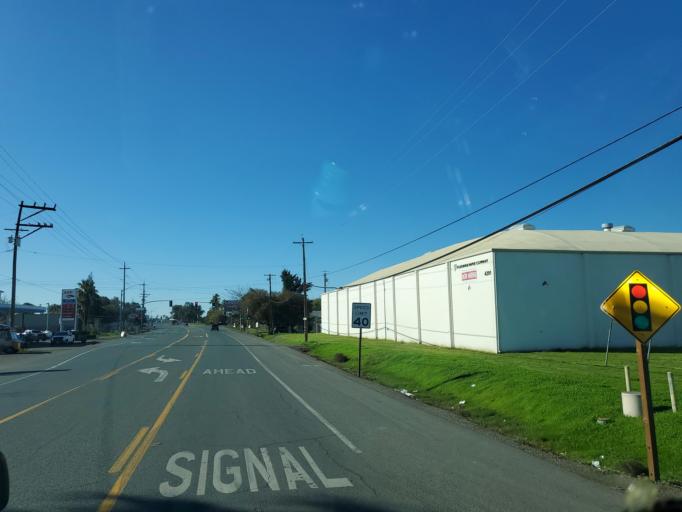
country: US
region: California
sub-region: San Joaquin County
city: Garden Acres
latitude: 37.9720
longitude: -121.2400
